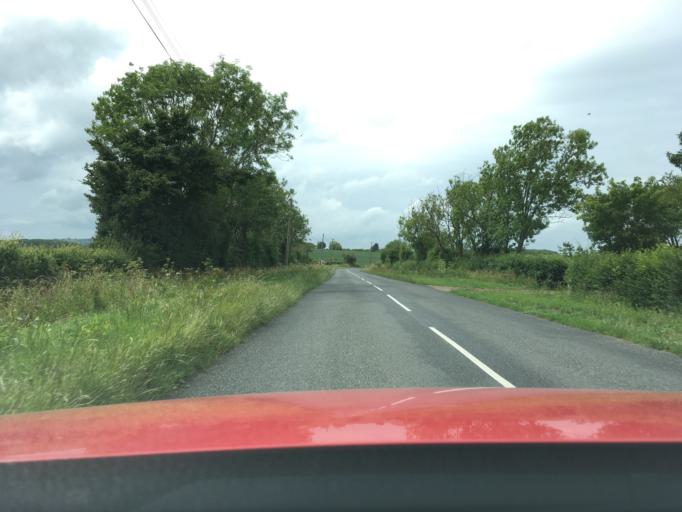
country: GB
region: England
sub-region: Worcestershire
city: Badsey
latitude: 52.0511
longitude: -1.9165
